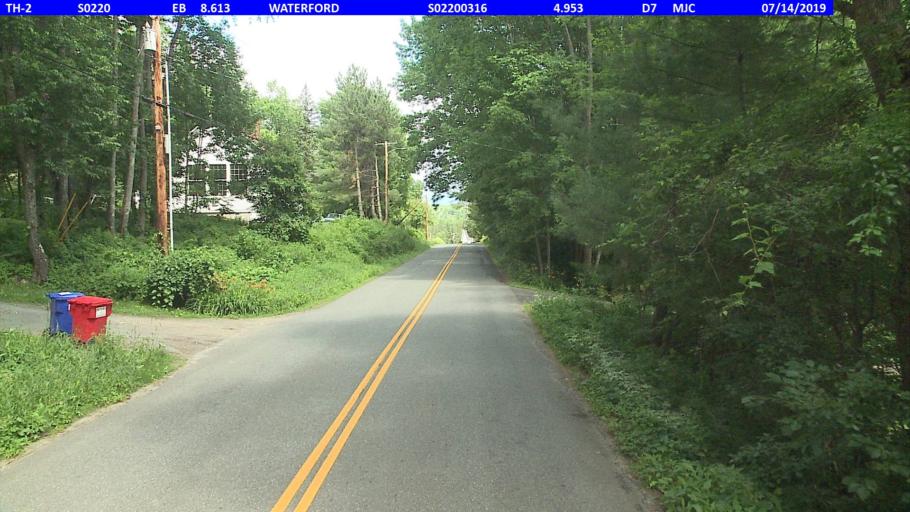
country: US
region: Vermont
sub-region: Caledonia County
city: Saint Johnsbury
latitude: 44.3543
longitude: -71.9118
